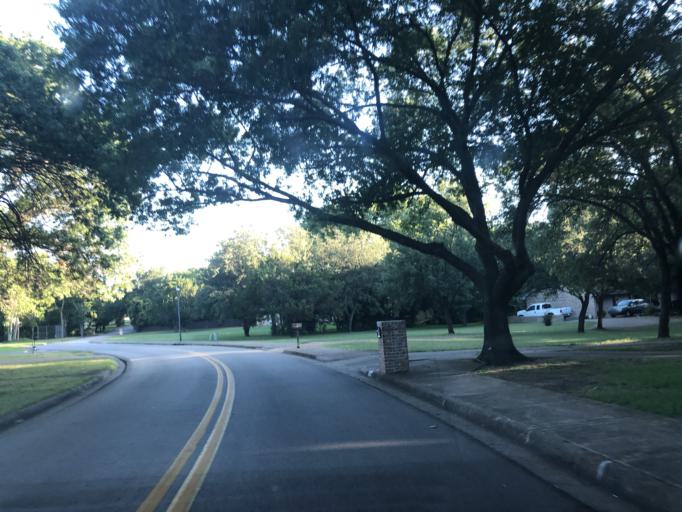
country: US
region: Texas
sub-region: Dallas County
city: Duncanville
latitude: 32.6360
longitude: -96.9339
